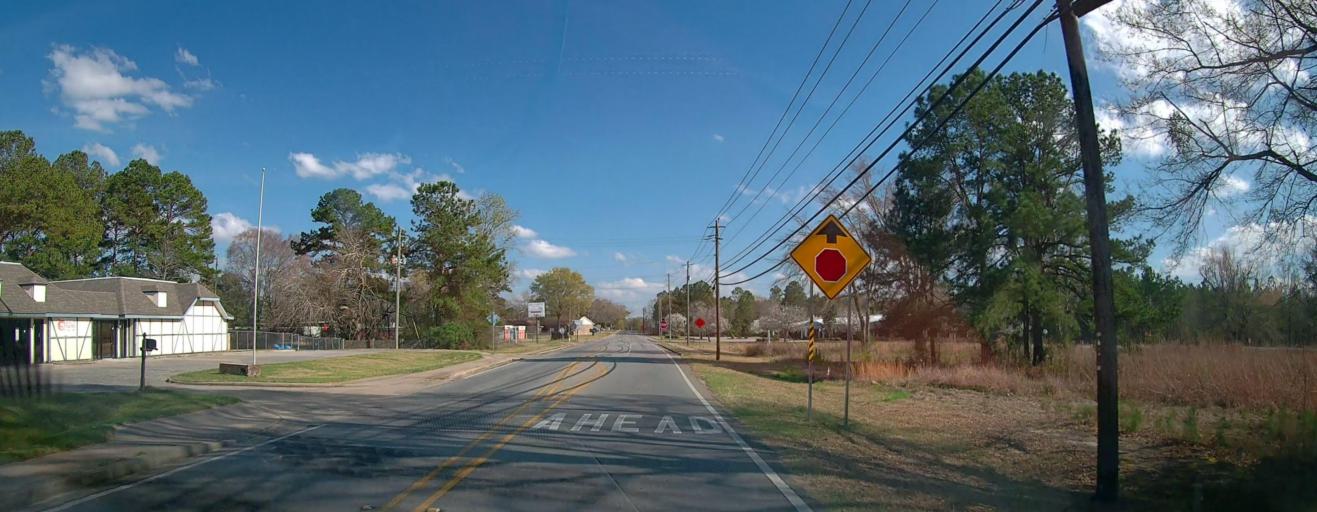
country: US
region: Georgia
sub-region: Laurens County
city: Dublin
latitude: 32.5456
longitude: -82.9219
